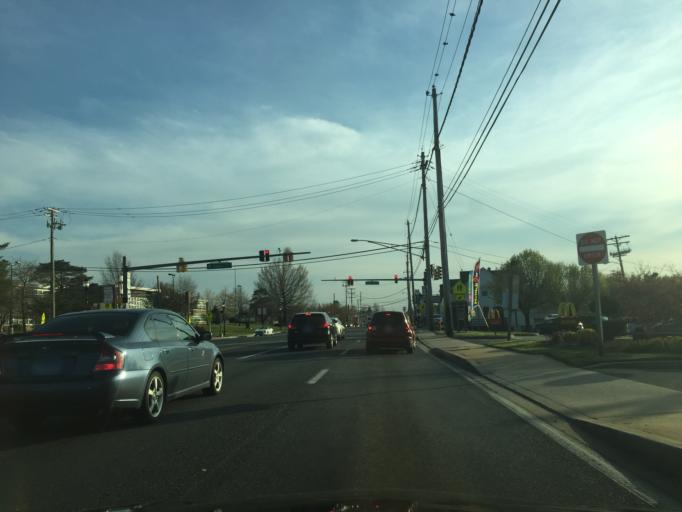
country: US
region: Maryland
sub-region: Baltimore County
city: Perry Hall
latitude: 39.4008
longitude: -76.4780
